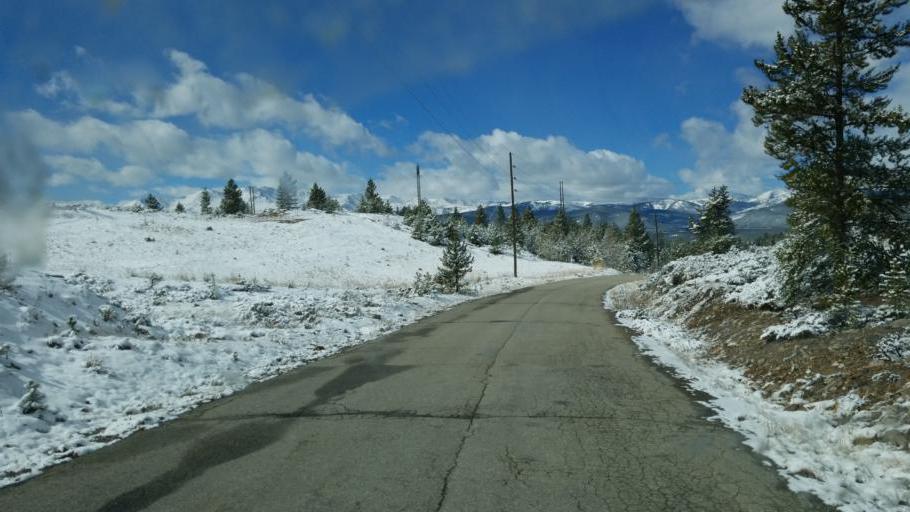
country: US
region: Colorado
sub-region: Lake County
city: Leadville
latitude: 39.2522
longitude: -106.2741
